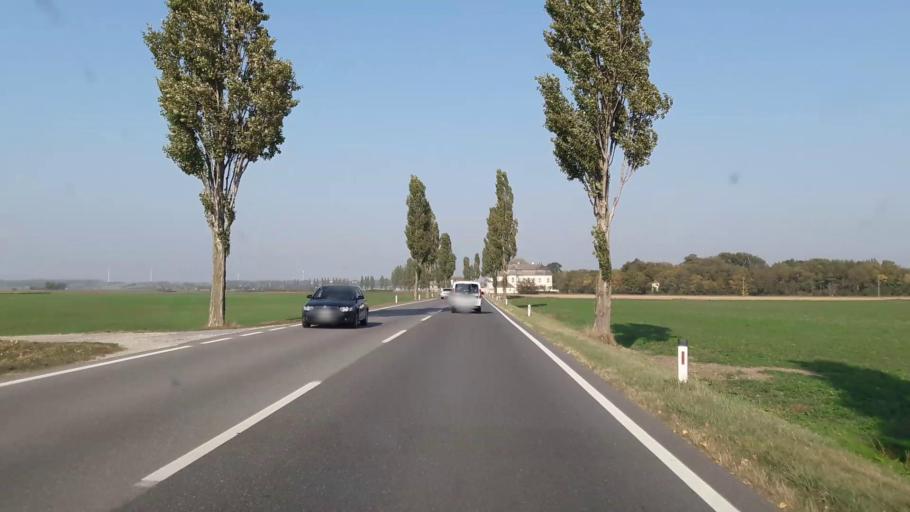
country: AT
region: Lower Austria
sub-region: Politischer Bezirk Ganserndorf
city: Engelhartstetten
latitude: 48.1936
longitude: 16.8985
